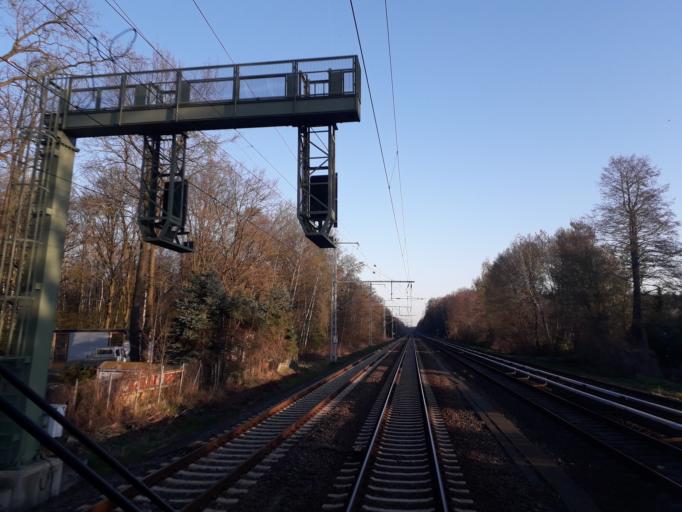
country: DE
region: Brandenburg
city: Zeuthen
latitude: 52.3763
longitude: 13.6119
